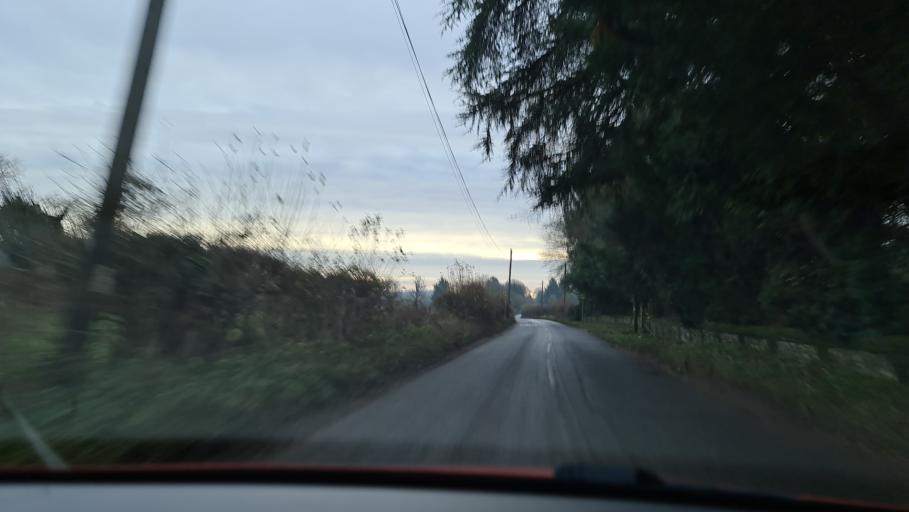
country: GB
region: England
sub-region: Buckinghamshire
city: Great Missenden
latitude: 51.7115
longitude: -0.7317
